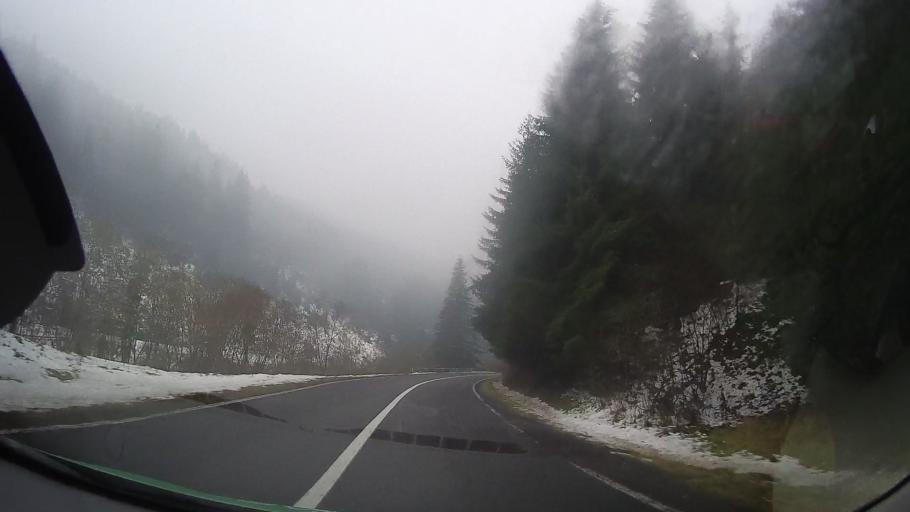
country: RO
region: Harghita
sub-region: Municipiul Gheorgheni
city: Gheorgheni
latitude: 46.7561
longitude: 25.6967
